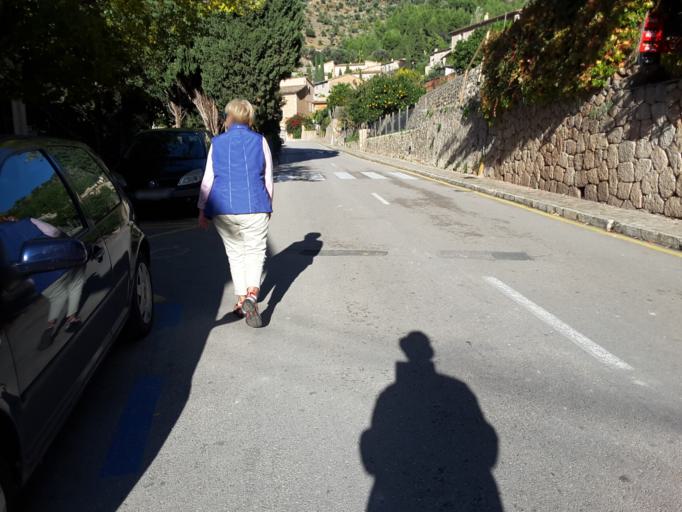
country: ES
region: Balearic Islands
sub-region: Illes Balears
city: Deia
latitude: 39.7477
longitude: 2.6485
